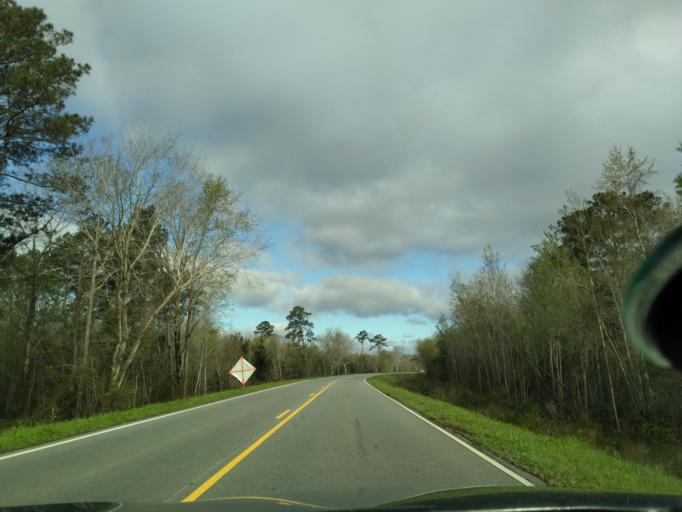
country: US
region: North Carolina
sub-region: Washington County
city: Plymouth
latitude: 35.9287
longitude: -76.7389
